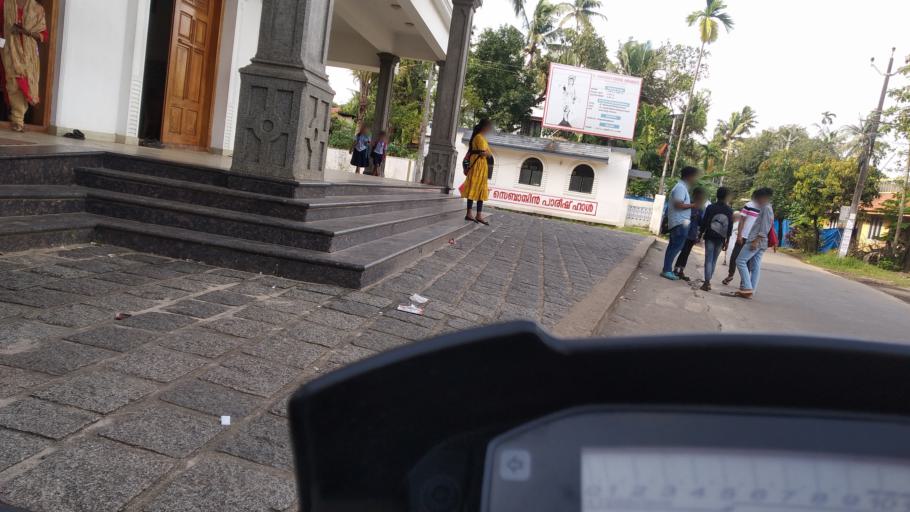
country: IN
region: Kerala
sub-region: Ernakulam
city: Cochin
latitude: 9.9953
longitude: 76.2646
